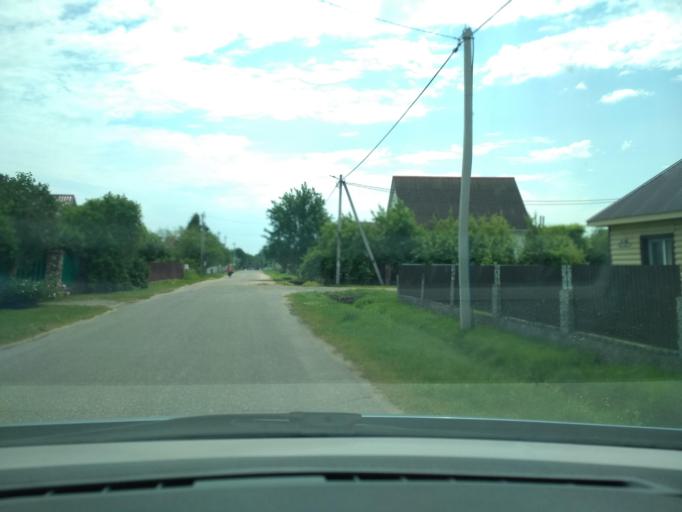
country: BY
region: Grodnenskaya
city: Astravyets
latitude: 54.6163
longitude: 25.9493
